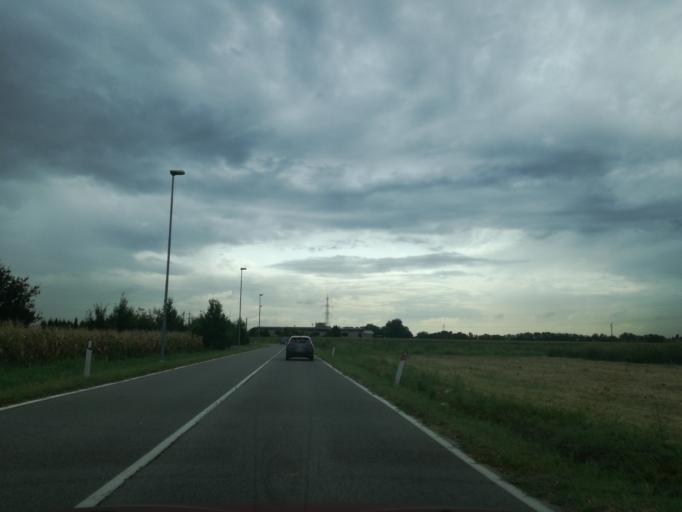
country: IT
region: Lombardy
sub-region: Provincia di Monza e Brianza
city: Mezzago
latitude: 45.6233
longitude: 9.4386
